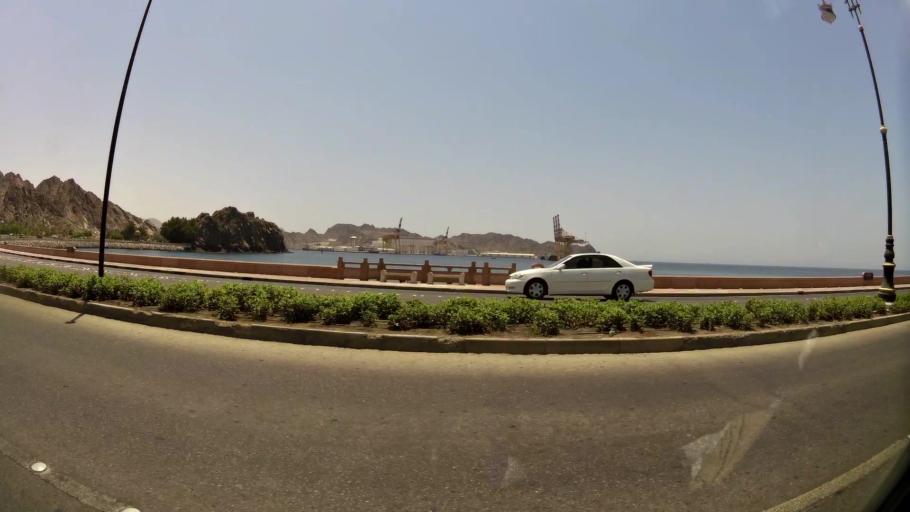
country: OM
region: Muhafazat Masqat
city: Muscat
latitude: 23.6227
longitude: 58.5771
